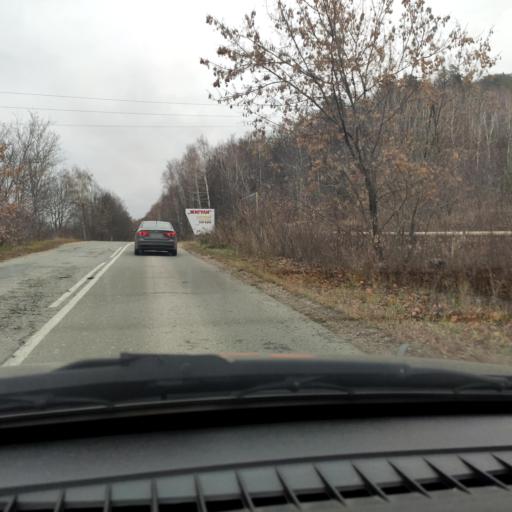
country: RU
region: Samara
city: Pribrezhnyy
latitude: 53.4384
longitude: 49.7278
